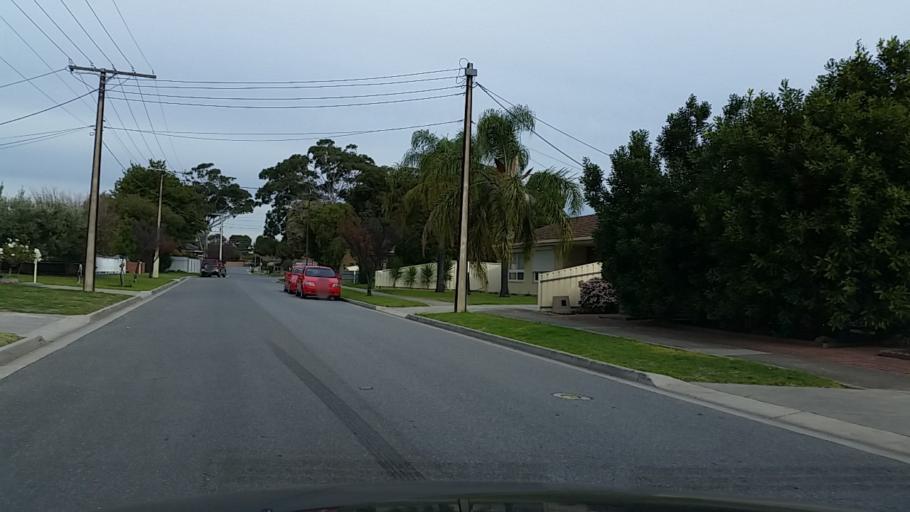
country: AU
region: South Australia
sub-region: Charles Sturt
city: Seaton
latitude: -34.9037
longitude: 138.5183
